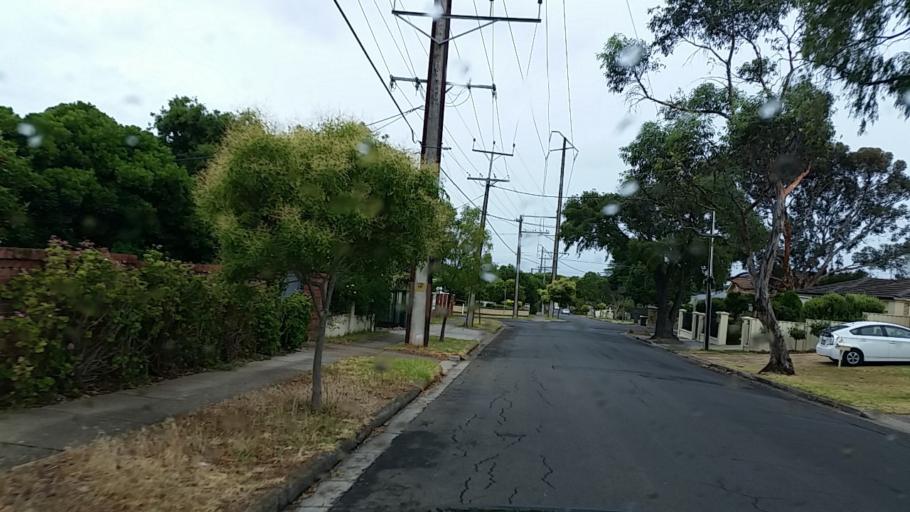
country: AU
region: South Australia
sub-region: Campbelltown
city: Campbelltown
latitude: -34.8977
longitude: 138.6820
